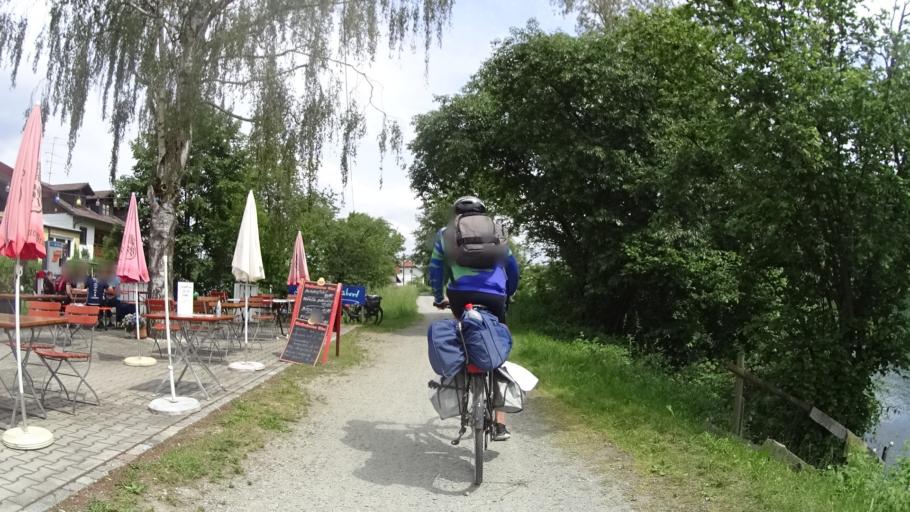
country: DE
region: Bavaria
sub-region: Lower Bavaria
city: Tiefenbach
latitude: 48.6037
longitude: 13.3241
